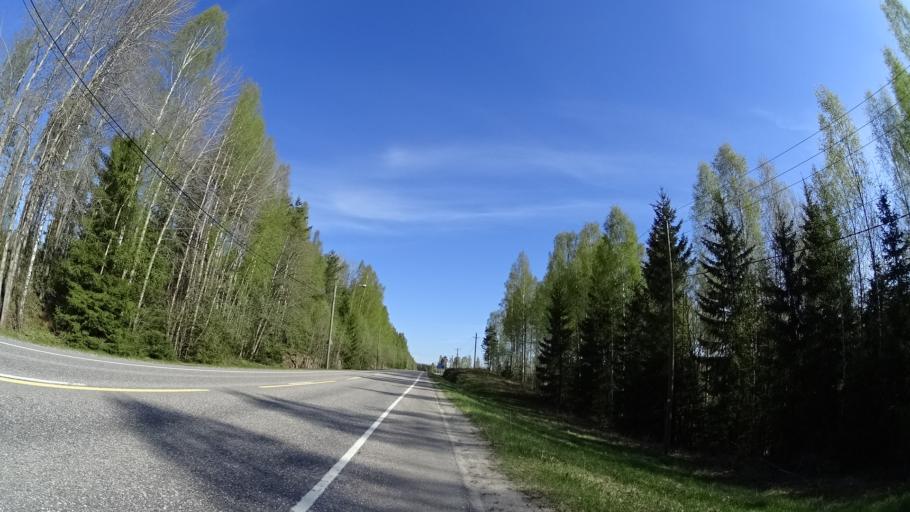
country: FI
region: Uusimaa
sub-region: Helsinki
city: Nurmijaervi
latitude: 60.3623
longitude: 24.8068
